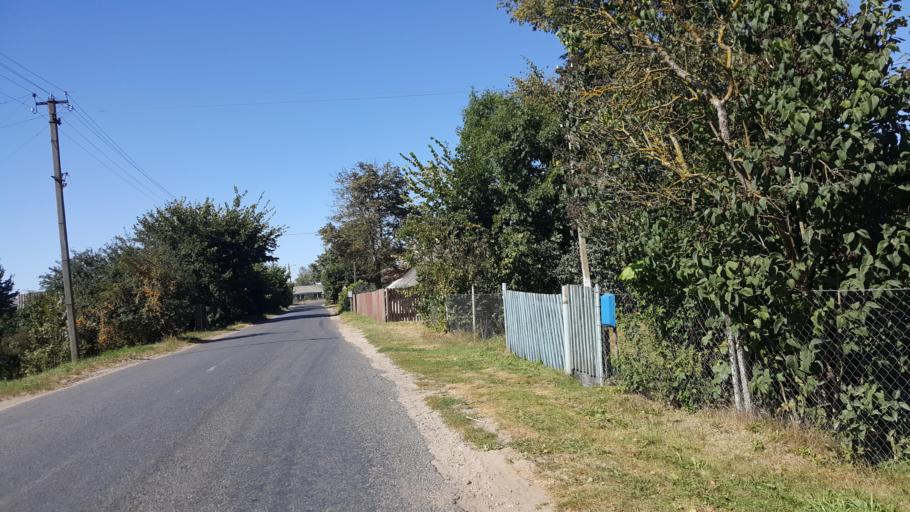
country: BY
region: Brest
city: Vysokaye
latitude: 52.2171
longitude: 23.4607
